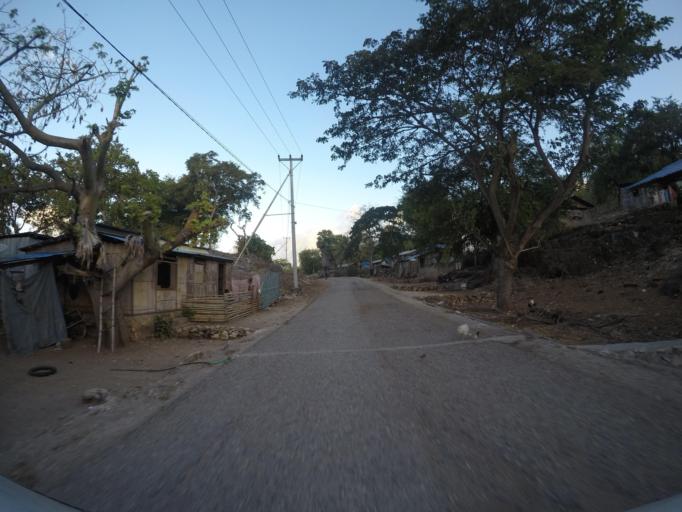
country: TL
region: Lautem
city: Lospalos
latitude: -8.3407
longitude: 127.0168
